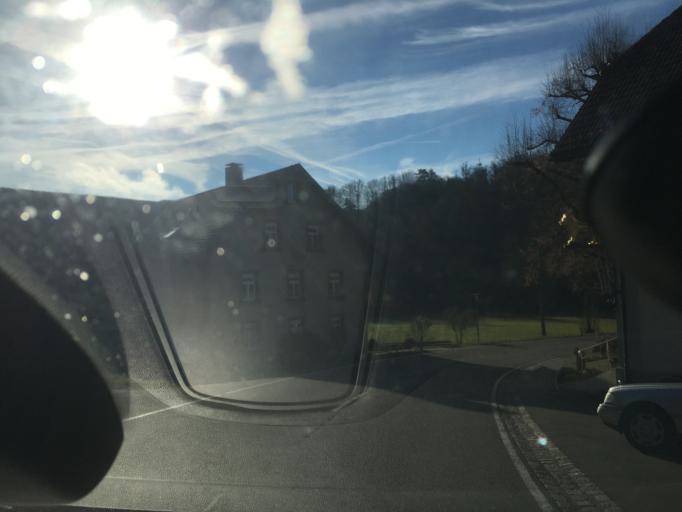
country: DE
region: Baden-Wuerttemberg
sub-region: Freiburg Region
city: Gorwihl
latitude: 47.6278
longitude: 8.0890
